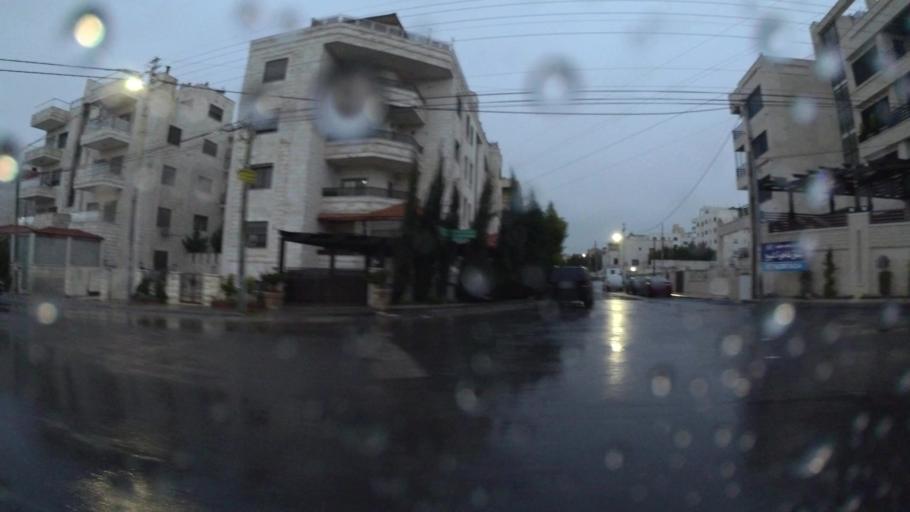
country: JO
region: Amman
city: Umm as Summaq
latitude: 31.9024
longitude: 35.8618
